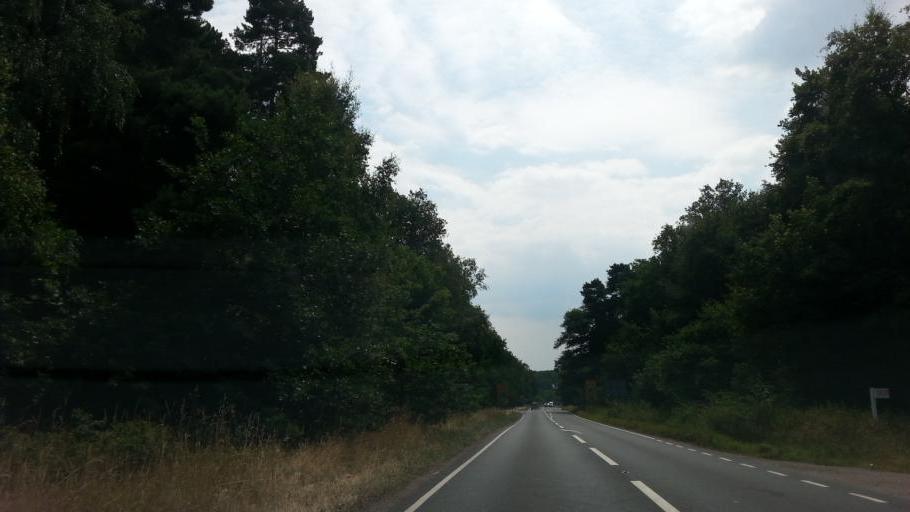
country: GB
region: England
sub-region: Suffolk
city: Lakenheath
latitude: 52.3430
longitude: 0.5357
